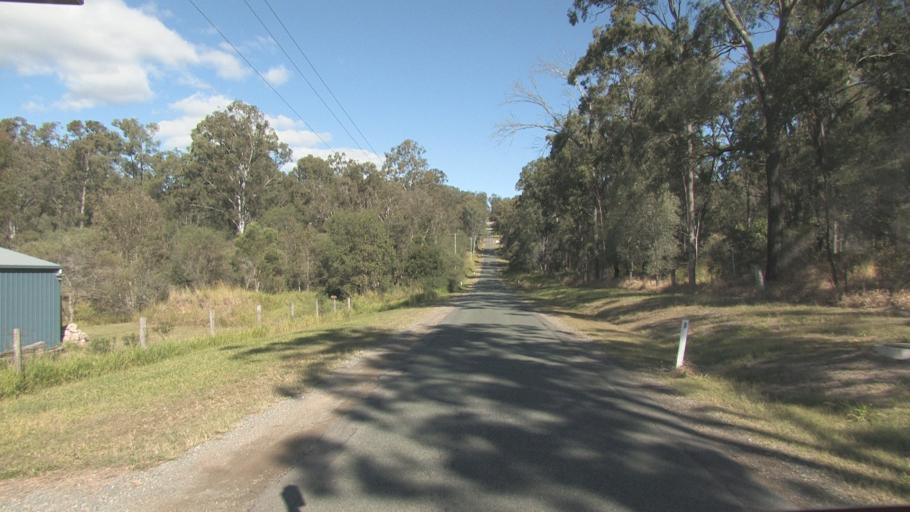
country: AU
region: Queensland
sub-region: Logan
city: Chambers Flat
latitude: -27.8065
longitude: 153.0826
